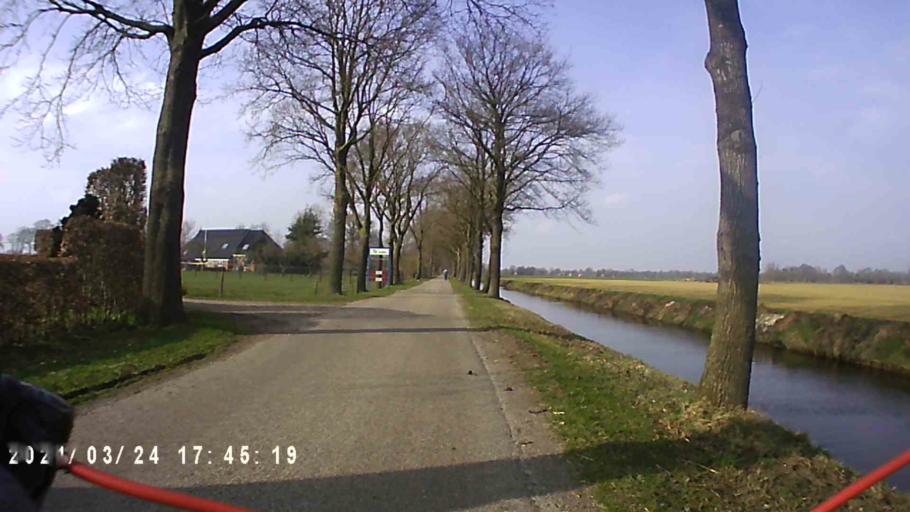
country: NL
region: Groningen
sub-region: Gemeente Leek
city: Leek
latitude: 53.1078
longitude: 6.3379
